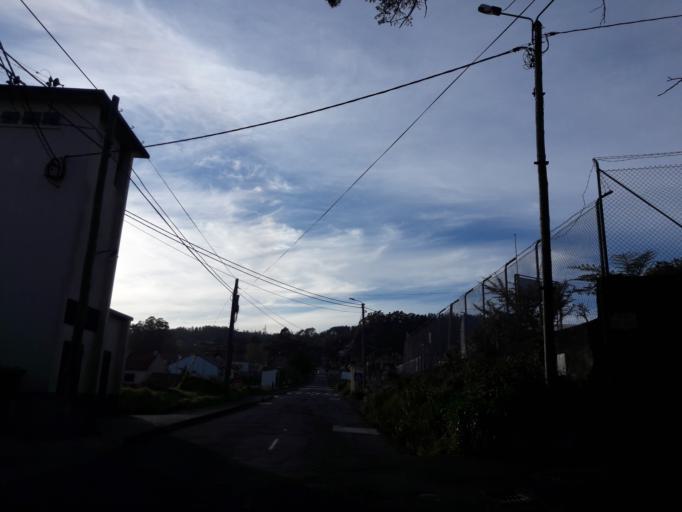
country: PT
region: Madeira
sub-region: Santa Cruz
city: Camacha
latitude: 32.6700
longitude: -16.8444
